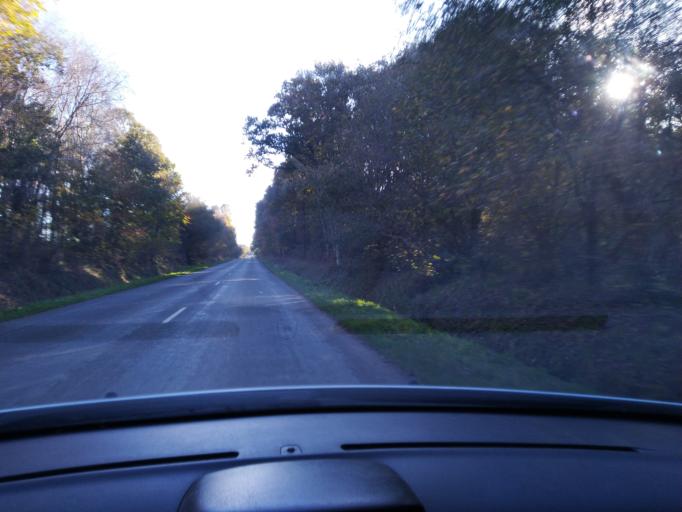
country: FR
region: Brittany
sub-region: Departement des Cotes-d'Armor
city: Plestin-les-Greves
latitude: 48.6167
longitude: -3.6199
